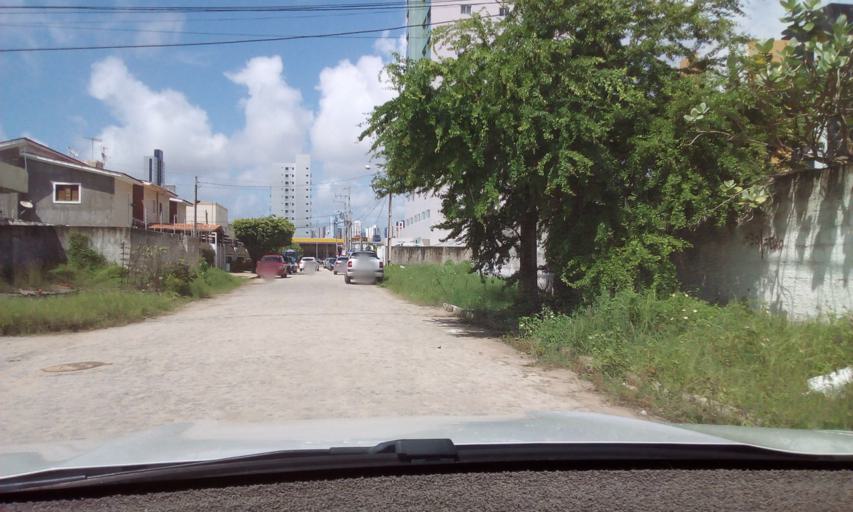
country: BR
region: Paraiba
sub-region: Joao Pessoa
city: Joao Pessoa
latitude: -7.0830
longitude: -34.8421
